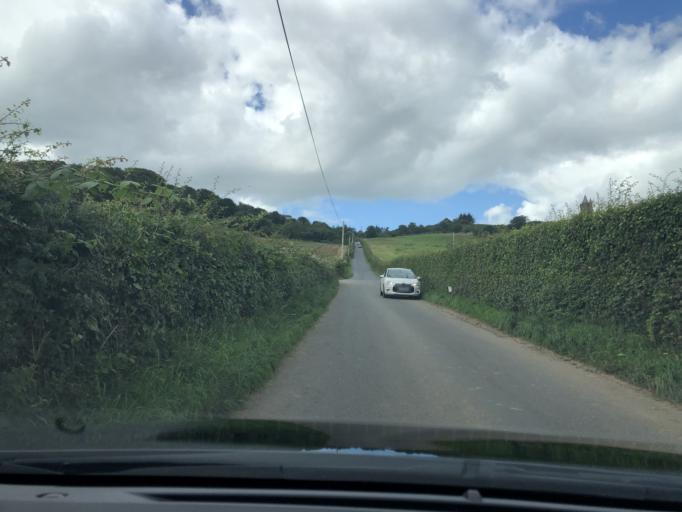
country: GB
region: Northern Ireland
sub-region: Ards District
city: Newtownards
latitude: 54.5741
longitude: -5.7162
